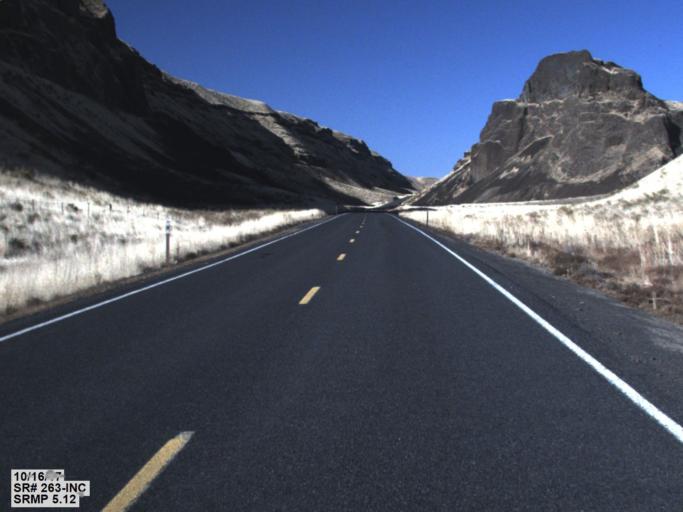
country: US
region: Washington
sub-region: Franklin County
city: Connell
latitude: 46.5891
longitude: -118.5439
